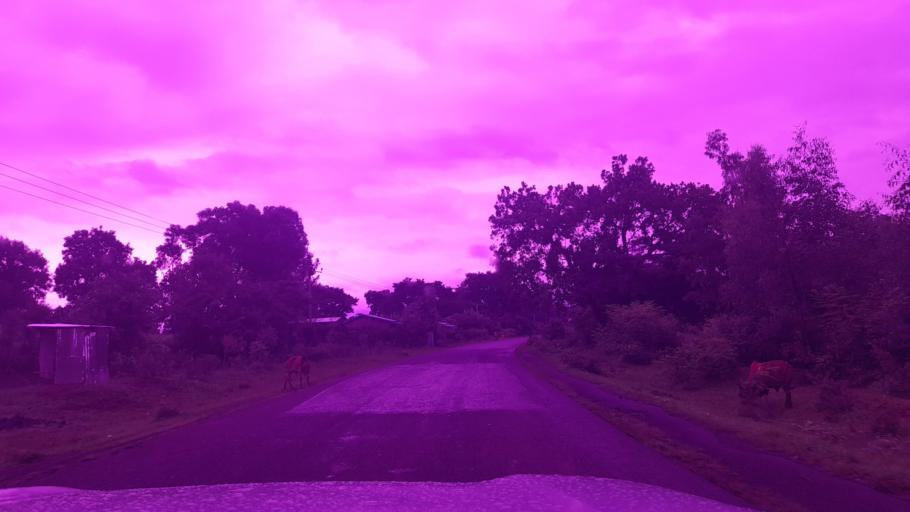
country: ET
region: Oromiya
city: Jima
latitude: 7.7090
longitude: 37.2528
